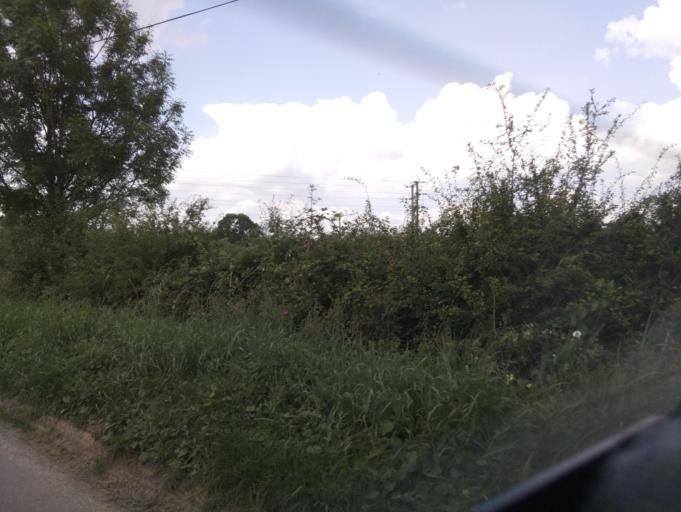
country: GB
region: England
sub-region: Wiltshire
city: Malmesbury
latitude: 51.5774
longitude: -2.1171
